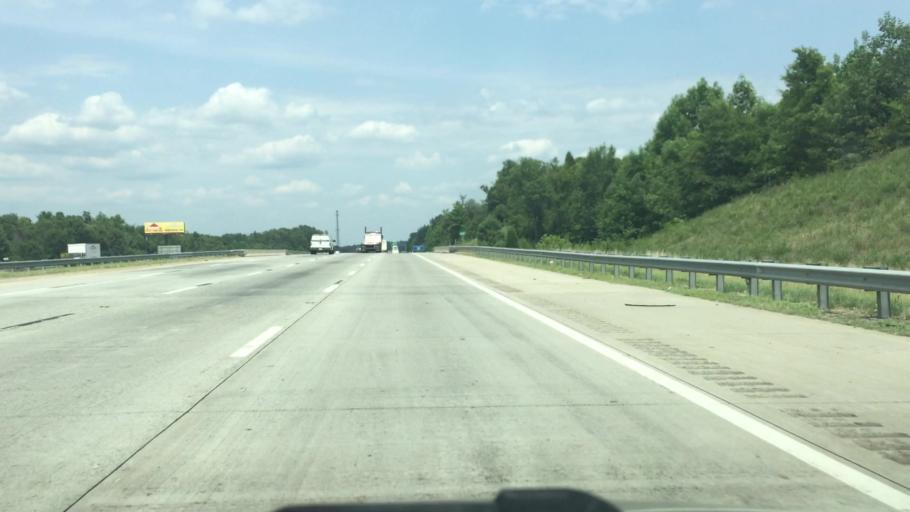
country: US
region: North Carolina
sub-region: Rowan County
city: East Spencer
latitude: 35.6696
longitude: -80.4341
